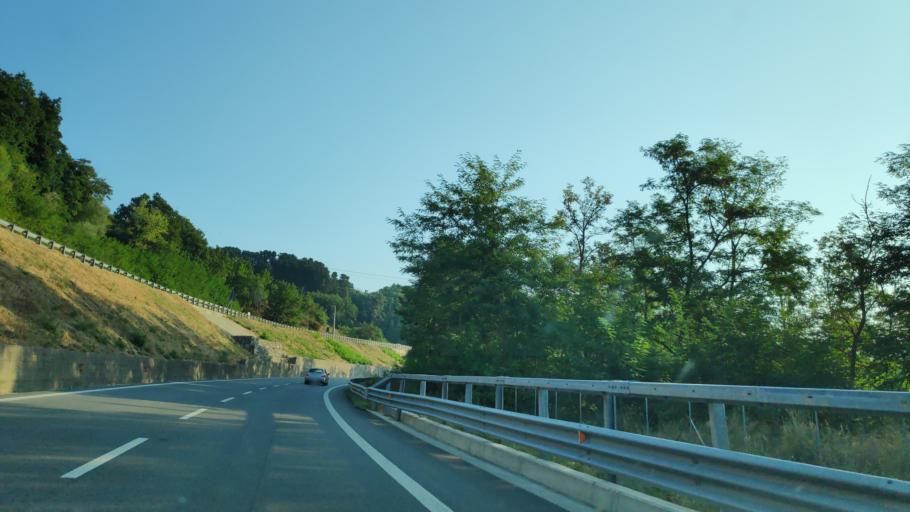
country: IT
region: Calabria
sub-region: Provincia di Cosenza
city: Belsito
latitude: 39.1613
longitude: 16.2871
